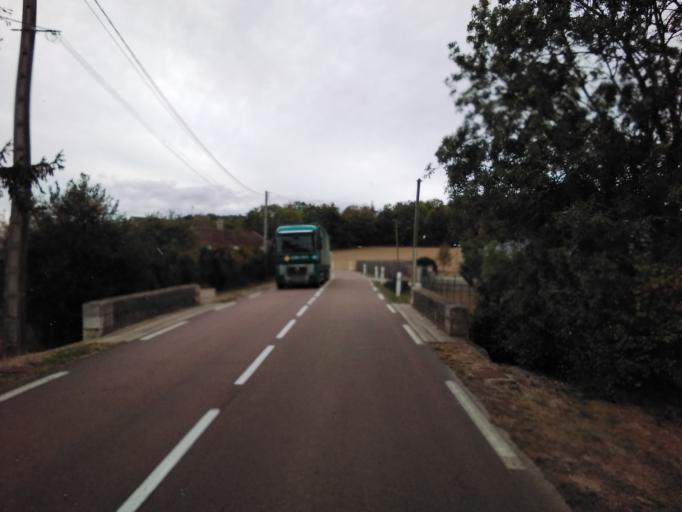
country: FR
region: Champagne-Ardenne
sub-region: Departement de l'Aube
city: Vendeuvre-sur-Barse
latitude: 48.1925
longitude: 4.4401
